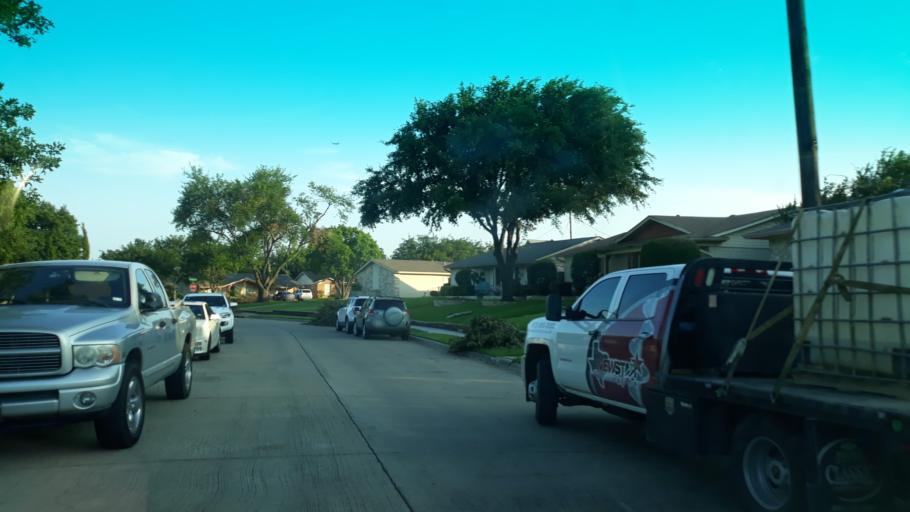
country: US
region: Texas
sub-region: Dallas County
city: Irving
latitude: 32.8520
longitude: -97.0044
